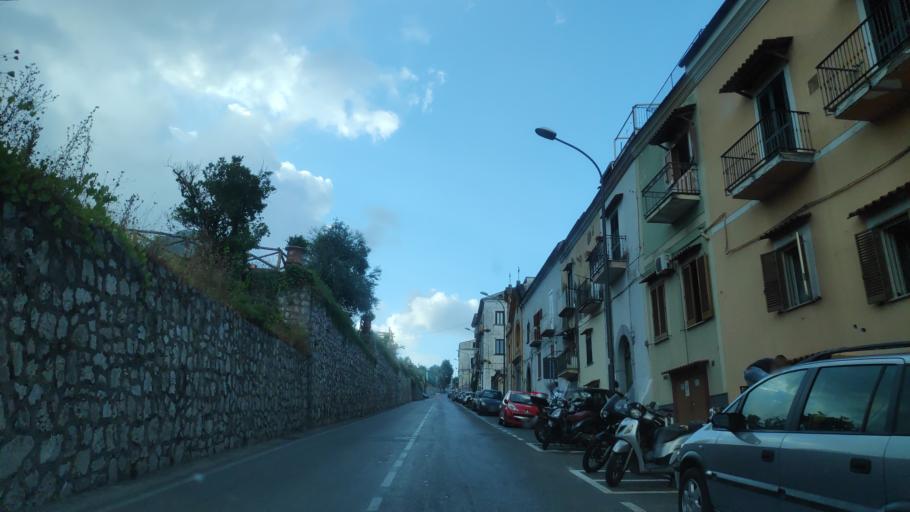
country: IT
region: Campania
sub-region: Provincia di Napoli
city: Piano di Sorrento
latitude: 40.6326
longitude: 14.4187
